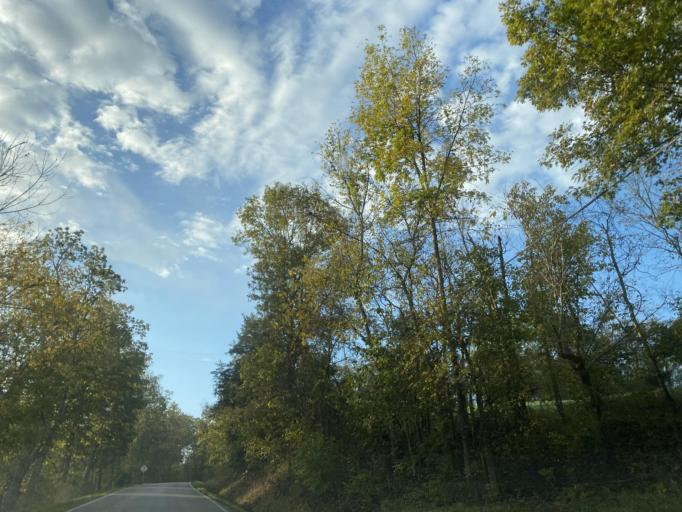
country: US
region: Kentucky
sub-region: Pendleton County
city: Falmouth
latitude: 38.7700
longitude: -84.3385
